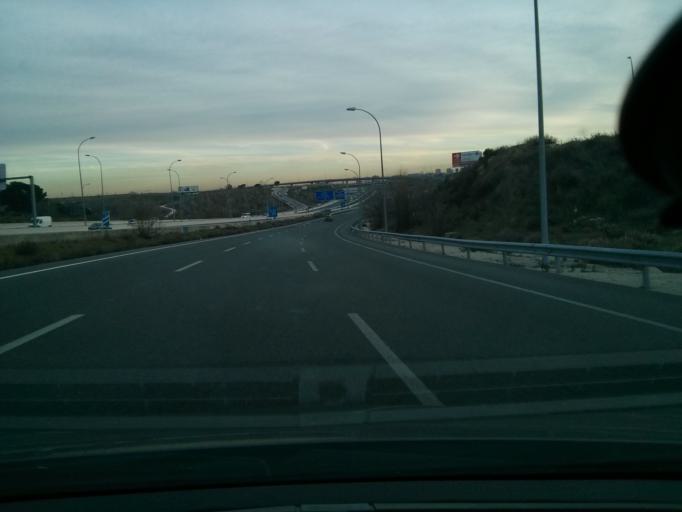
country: ES
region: Madrid
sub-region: Provincia de Madrid
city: Las Tablas
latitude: 40.5048
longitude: -3.6494
